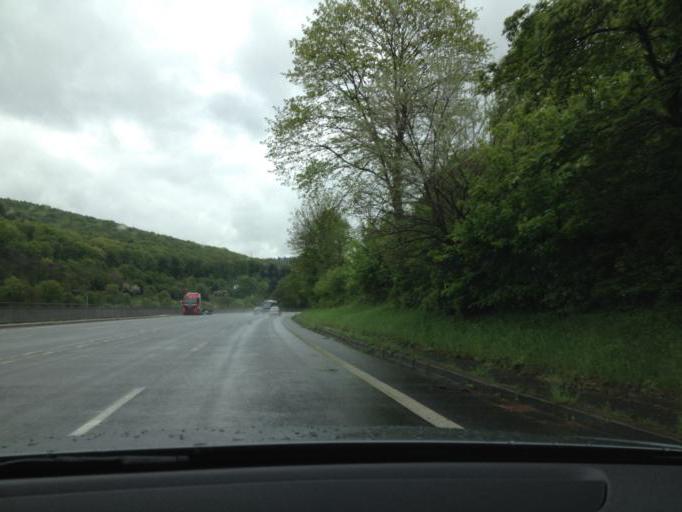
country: DE
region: Baden-Wuerttemberg
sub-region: Karlsruhe Region
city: Neckargemund
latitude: 49.4080
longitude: 8.7767
